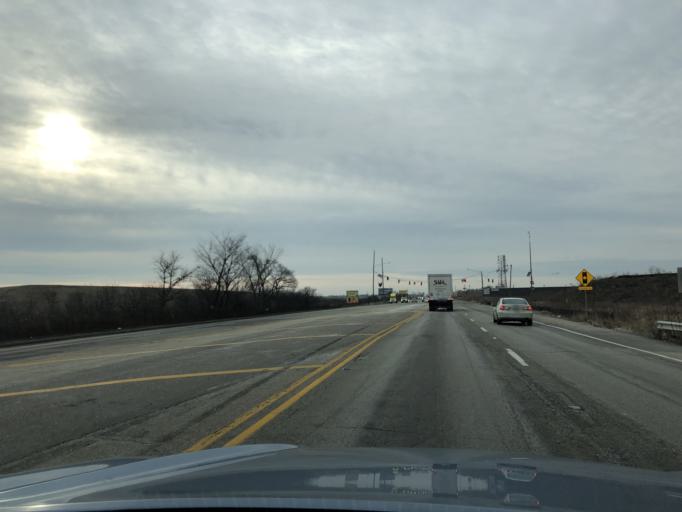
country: US
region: Illinois
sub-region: DuPage County
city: Bensenville
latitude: 41.9778
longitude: -87.9397
